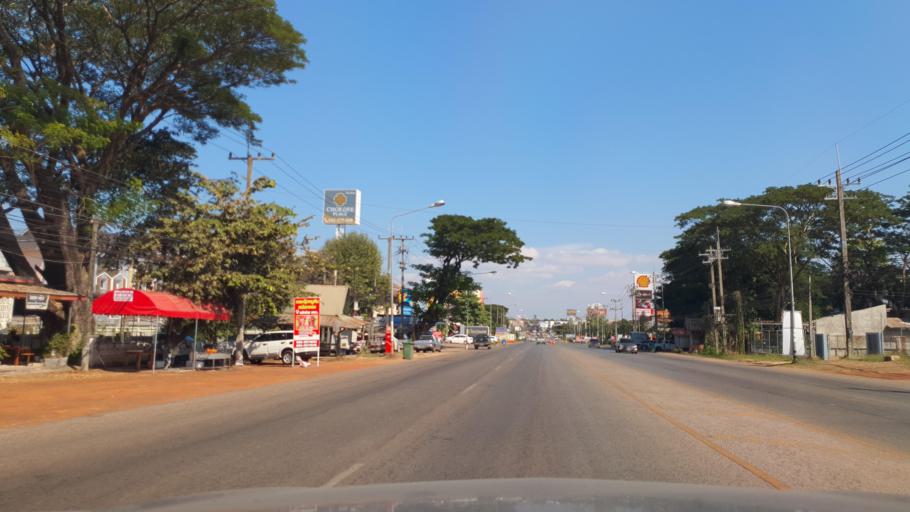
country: TH
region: Sakon Nakhon
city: Sakon Nakhon
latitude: 17.1457
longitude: 104.1233
